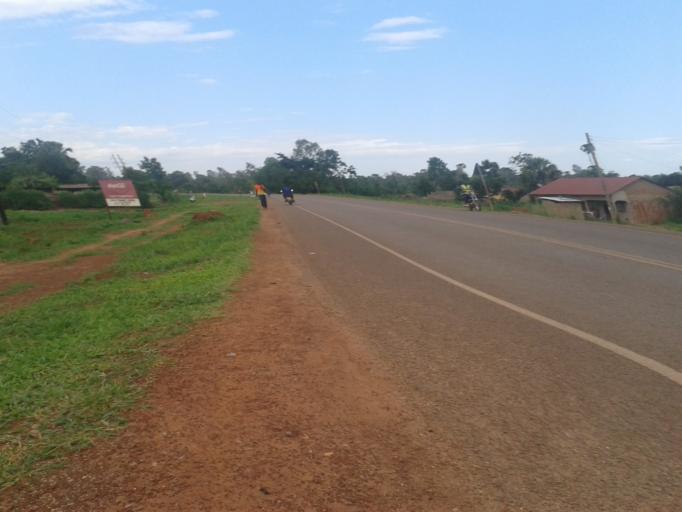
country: UG
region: Northern Region
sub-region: Gulu District
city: Gulu
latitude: 2.7634
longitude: 32.2721
